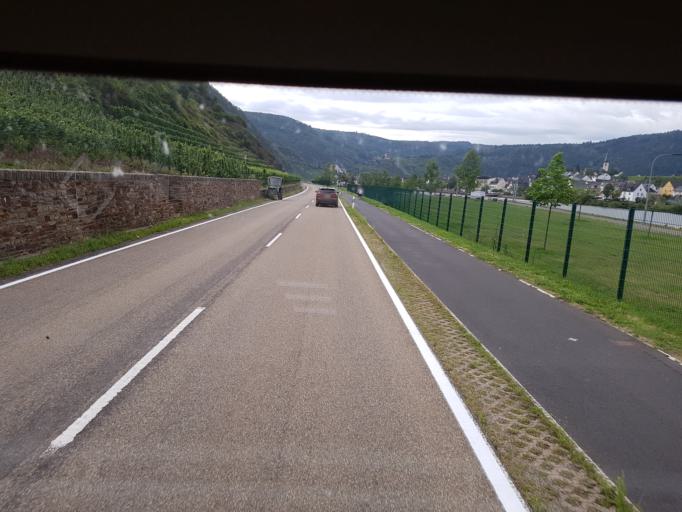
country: DE
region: Rheinland-Pfalz
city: Bruttig-Fankel
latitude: 50.1217
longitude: 7.2310
